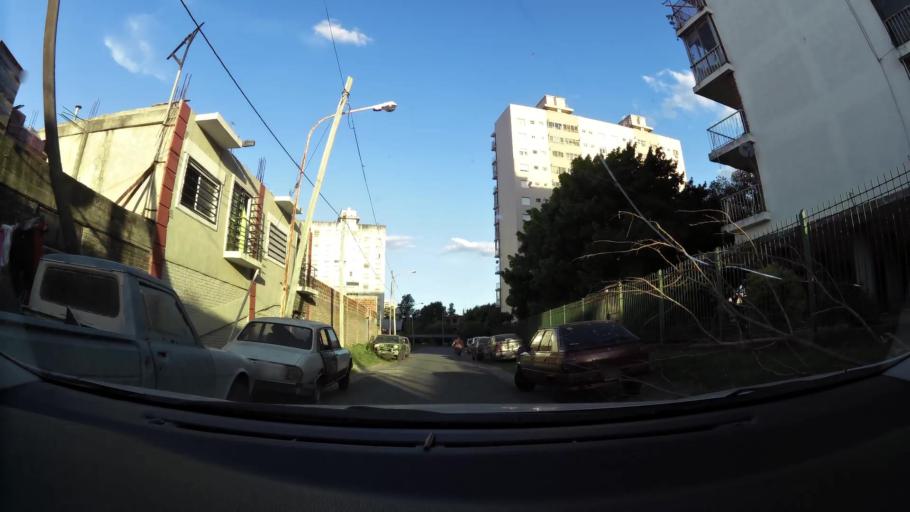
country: AR
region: Buenos Aires F.D.
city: Villa Lugano
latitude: -34.6977
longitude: -58.4809
